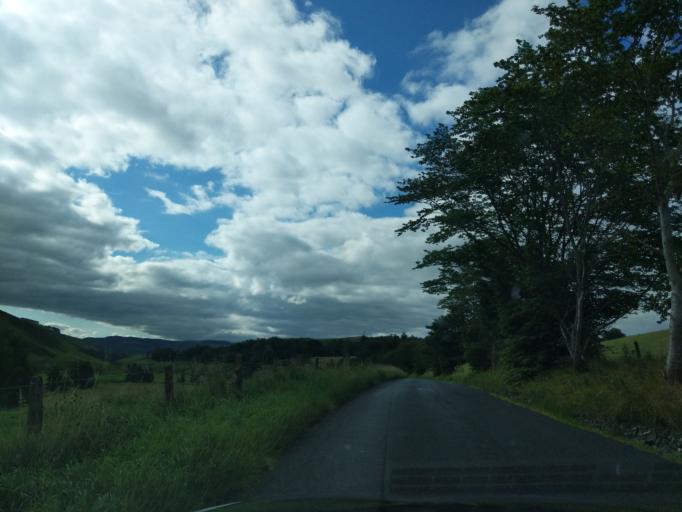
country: GB
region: Scotland
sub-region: The Scottish Borders
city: West Linton
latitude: 55.7053
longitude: -3.3385
